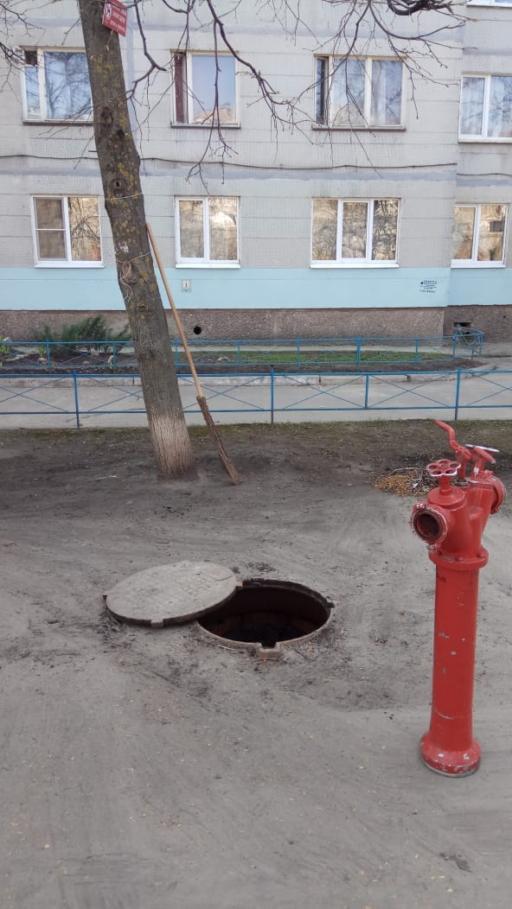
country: RU
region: Voronezj
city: Podgornoye
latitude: 51.7120
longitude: 39.1671
